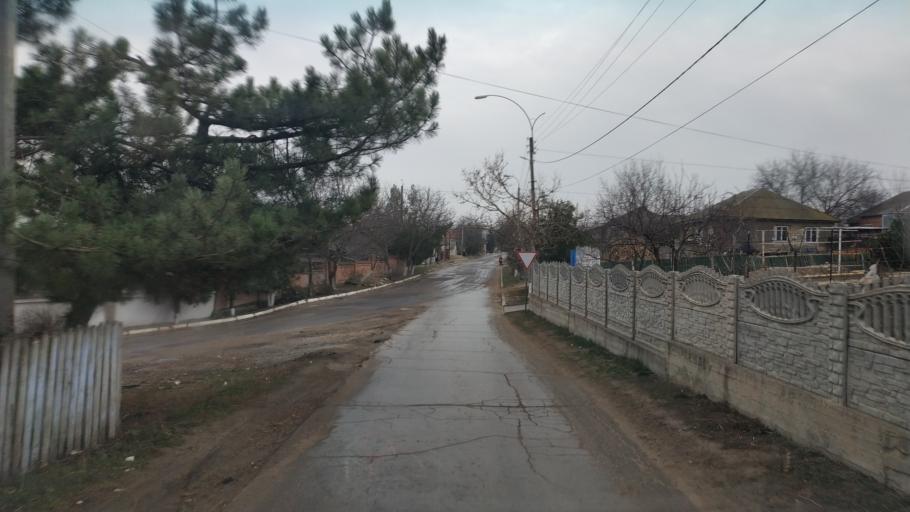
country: MD
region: Chisinau
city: Singera
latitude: 46.8268
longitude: 28.9726
